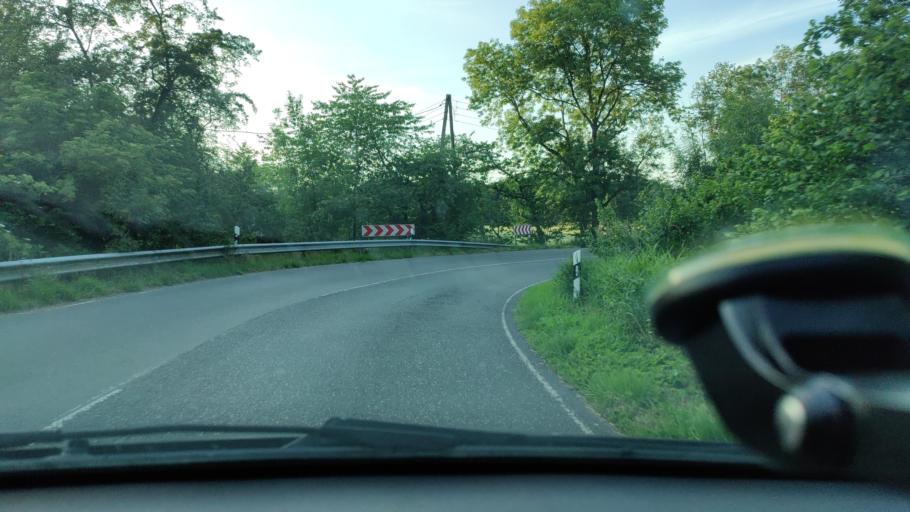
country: DE
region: North Rhine-Westphalia
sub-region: Regierungsbezirk Dusseldorf
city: Kamp-Lintfort
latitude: 51.4873
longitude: 6.5168
